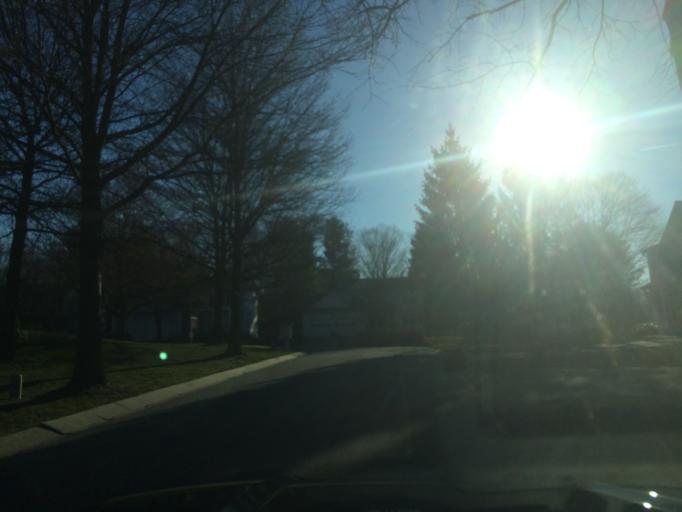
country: US
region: Maryland
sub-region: Howard County
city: Riverside
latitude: 39.2011
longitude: -76.8951
